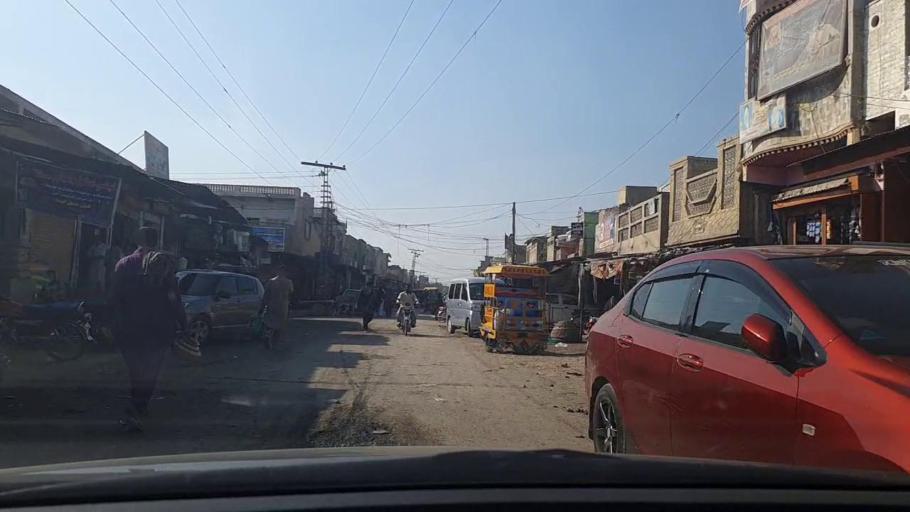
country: PK
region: Sindh
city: Sakrand
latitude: 26.3018
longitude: 68.1011
